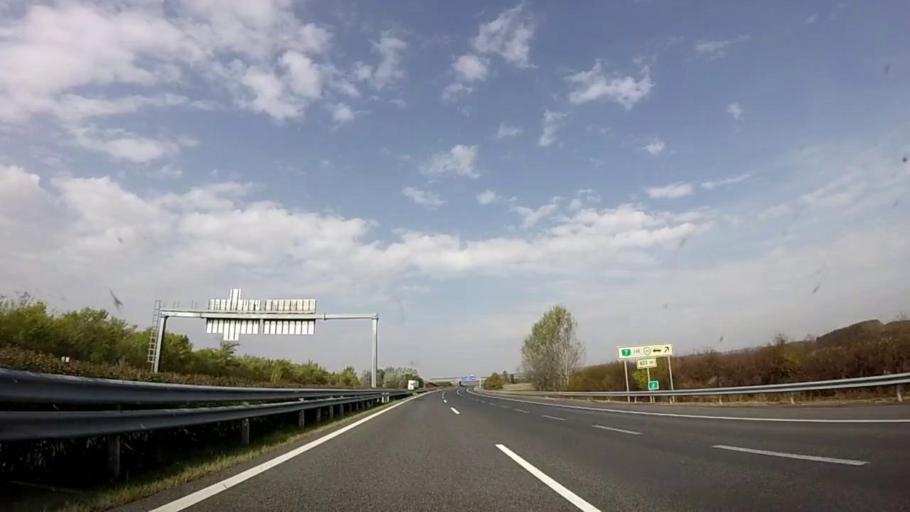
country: HU
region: Zala
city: Letenye
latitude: 46.4200
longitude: 16.7139
